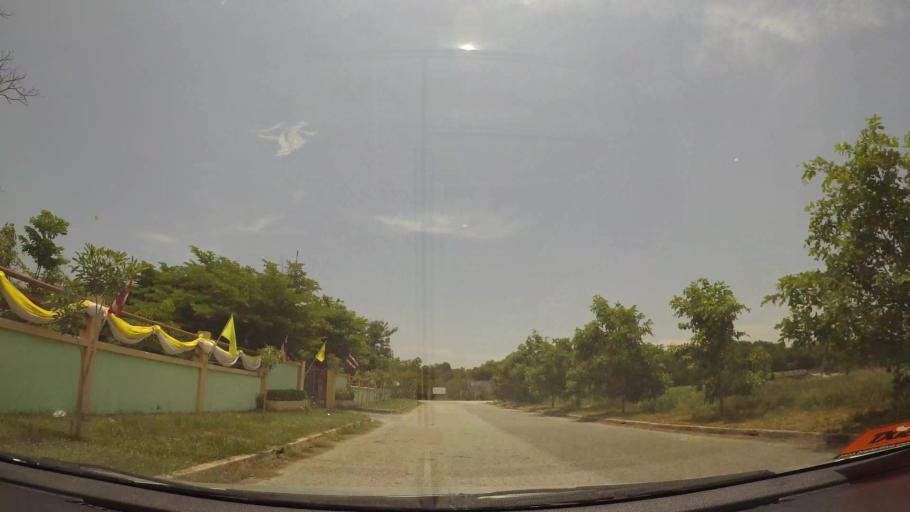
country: TH
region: Chon Buri
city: Chon Buri
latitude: 13.3456
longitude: 100.9550
